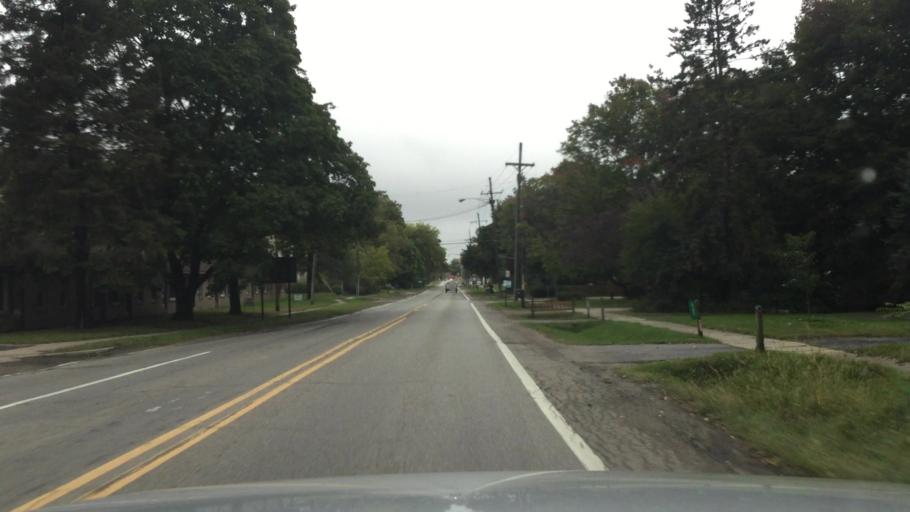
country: US
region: Michigan
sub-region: Oakland County
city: Waterford
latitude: 42.6996
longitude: -83.4078
